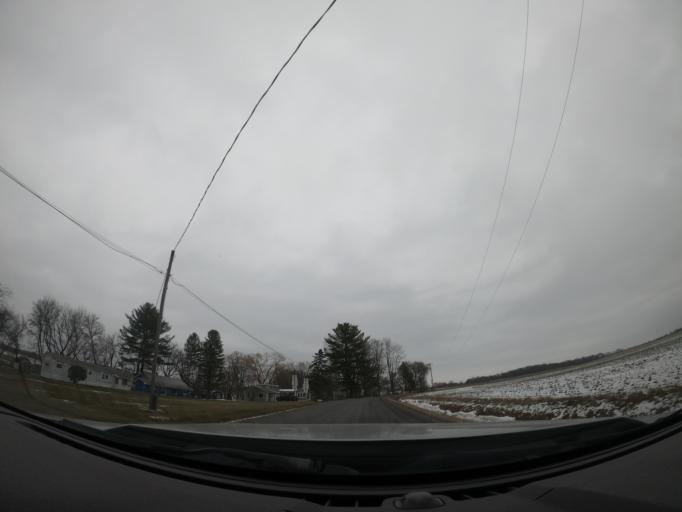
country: US
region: New York
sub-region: Cayuga County
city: Moravia
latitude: 42.6355
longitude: -76.4936
